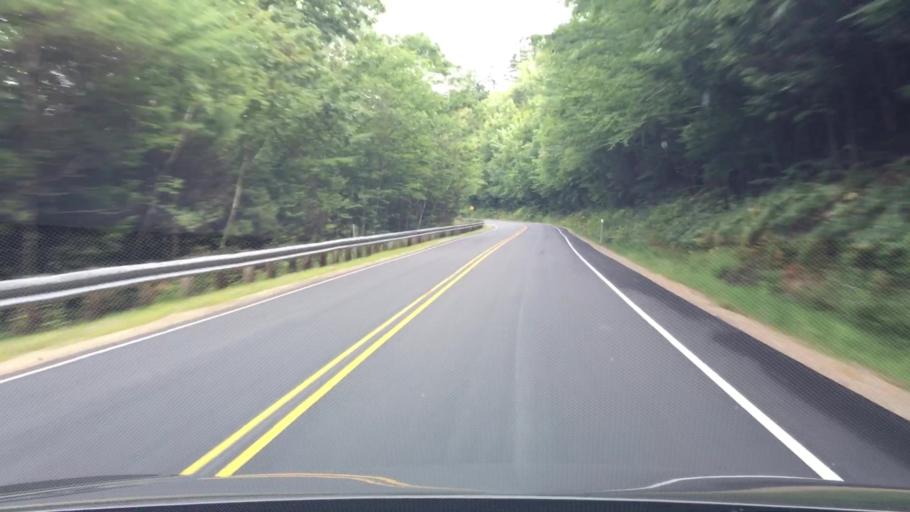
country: US
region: New Hampshire
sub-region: Carroll County
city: Conway
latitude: 43.9902
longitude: -71.1677
